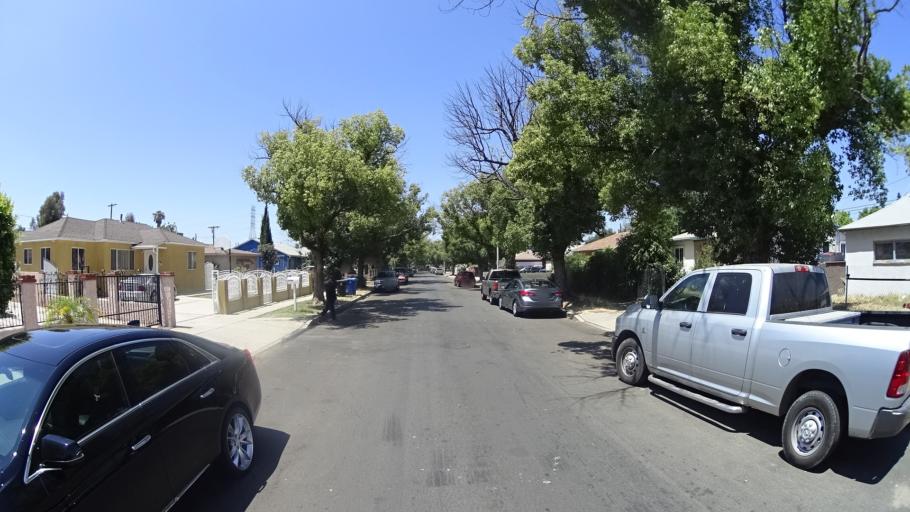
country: US
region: California
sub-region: Los Angeles County
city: San Fernando
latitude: 34.2378
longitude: -118.4289
